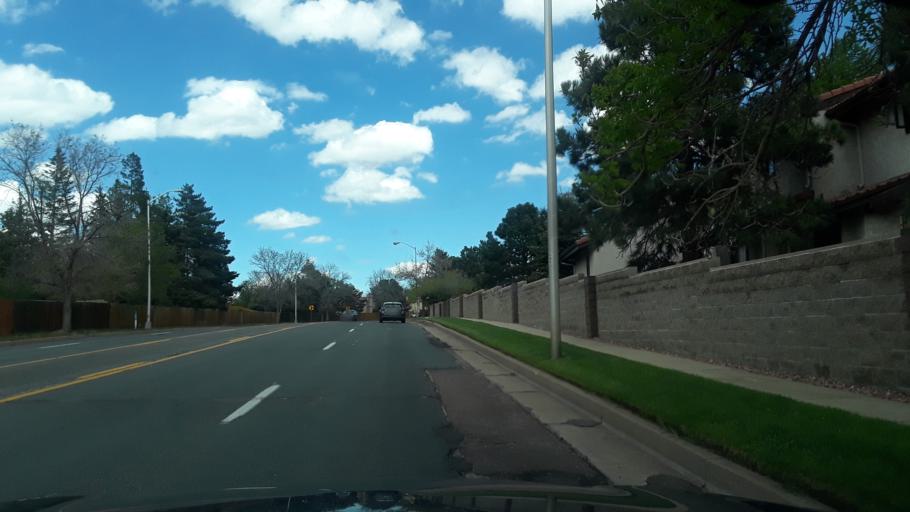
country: US
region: Colorado
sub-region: El Paso County
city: Black Forest
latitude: 38.9419
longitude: -104.7718
